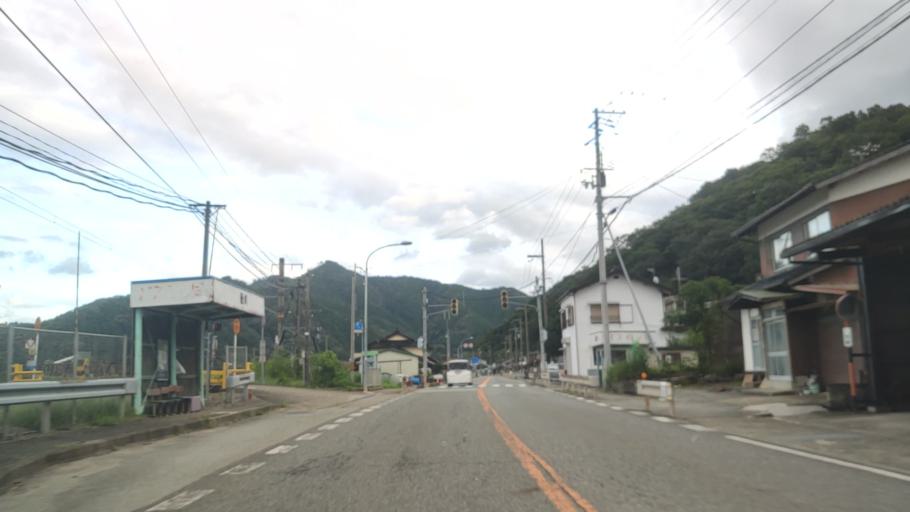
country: JP
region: Hyogo
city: Toyooka
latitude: 35.3952
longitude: 134.7859
